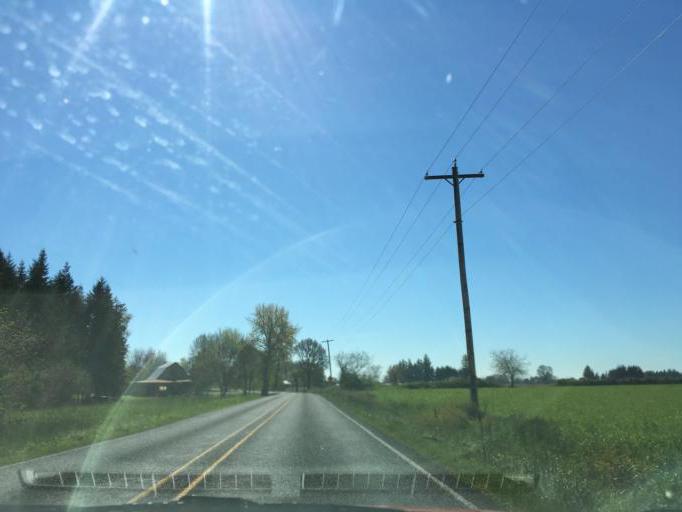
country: US
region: Oregon
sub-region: Marion County
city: Hubbard
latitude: 45.1483
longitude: -122.7269
